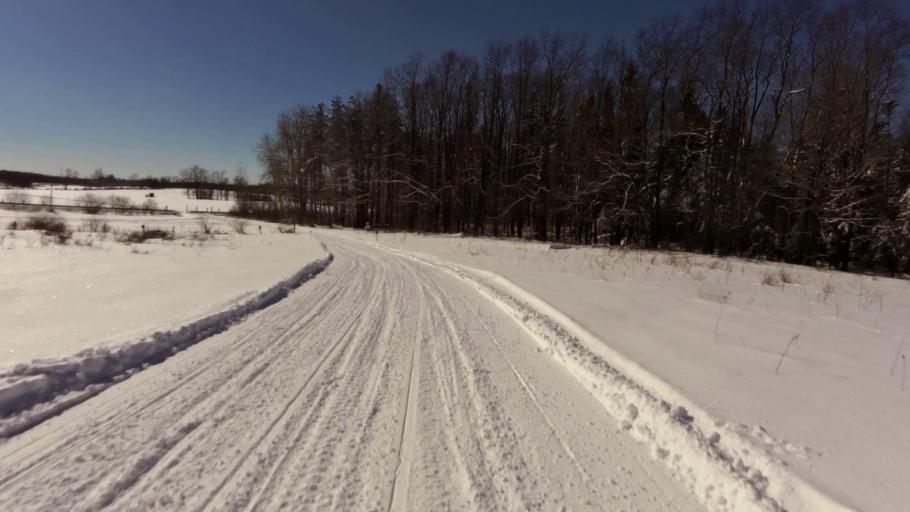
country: US
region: New York
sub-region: Chautauqua County
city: Mayville
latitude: 42.2289
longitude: -79.3934
